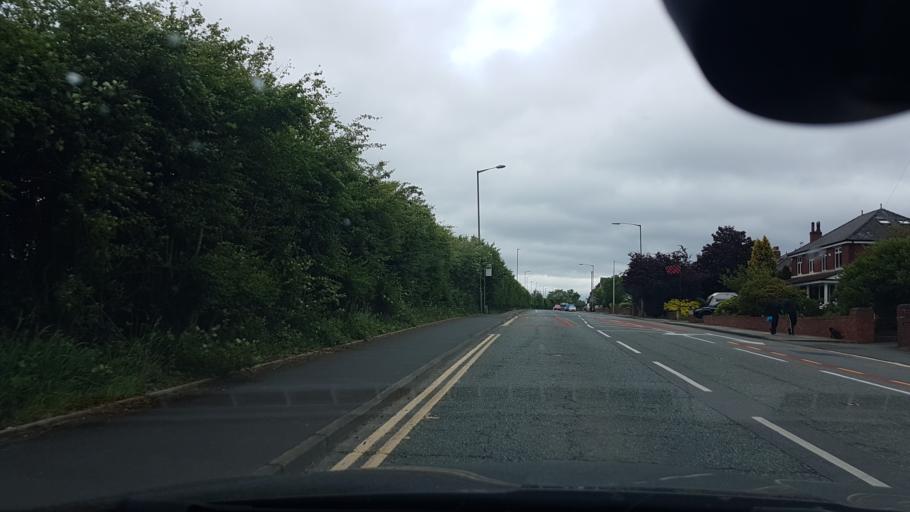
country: GB
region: England
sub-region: Borough of Bury
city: Radcliffe
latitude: 53.5830
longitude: -2.3336
